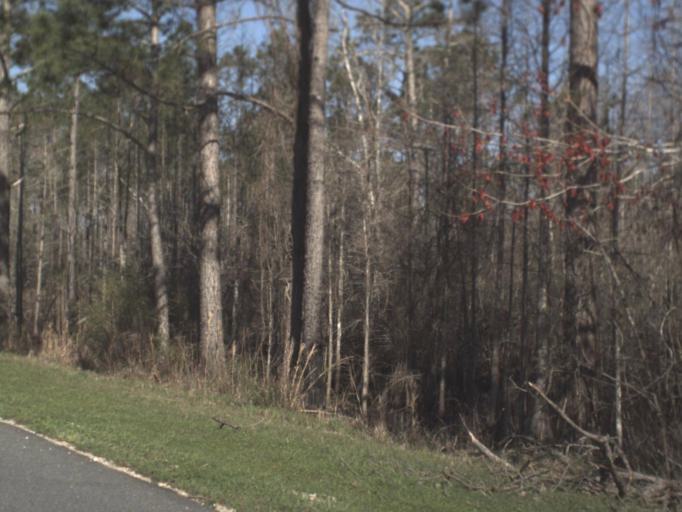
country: US
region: Florida
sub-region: Leon County
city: Woodville
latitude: 30.1876
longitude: -84.0254
